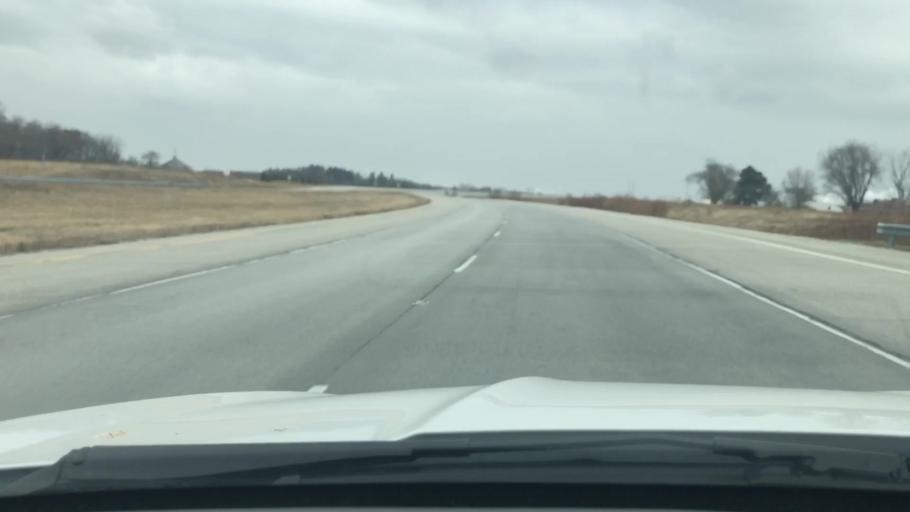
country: US
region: Indiana
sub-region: Cass County
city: Georgetown
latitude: 40.7042
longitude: -86.4570
